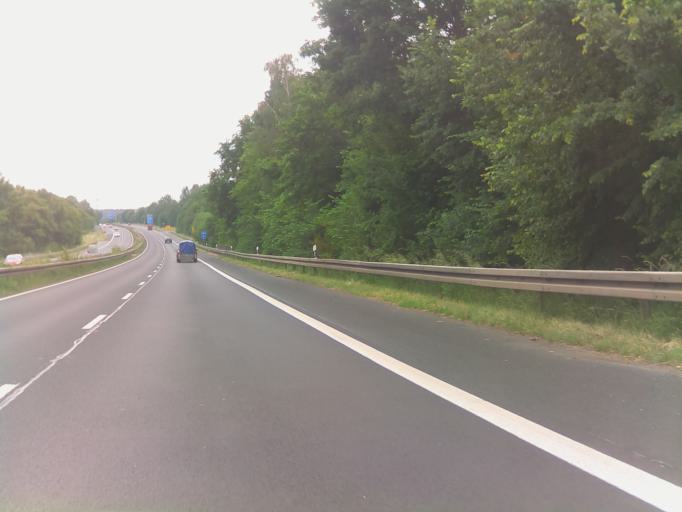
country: DE
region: Hesse
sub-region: Regierungsbezirk Kassel
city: Eichenzell
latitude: 50.5000
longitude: 9.6852
